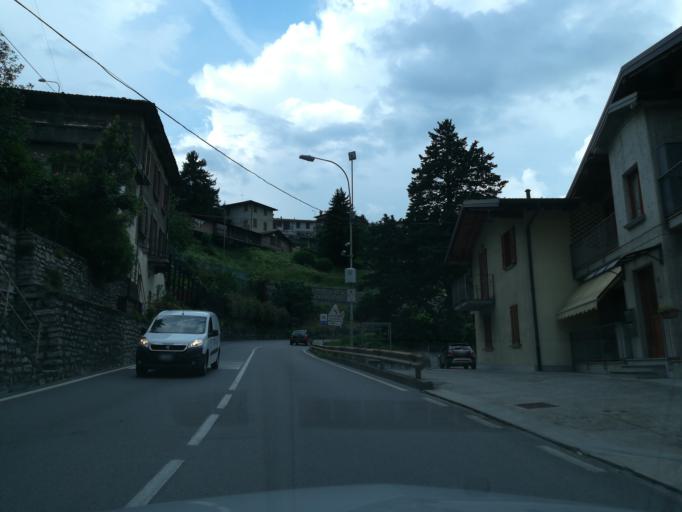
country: IT
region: Lombardy
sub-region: Provincia di Bergamo
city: Almenno San Salvatore
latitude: 45.7509
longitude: 9.6024
